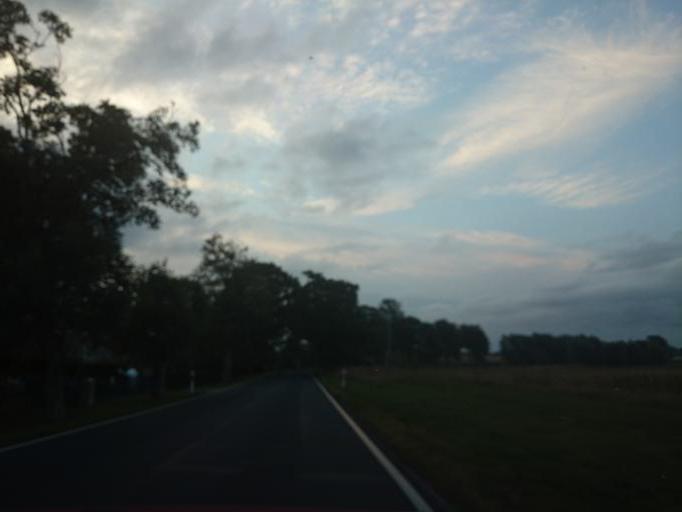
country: DE
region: Mecklenburg-Vorpommern
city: Barth
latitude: 54.3427
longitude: 12.7801
